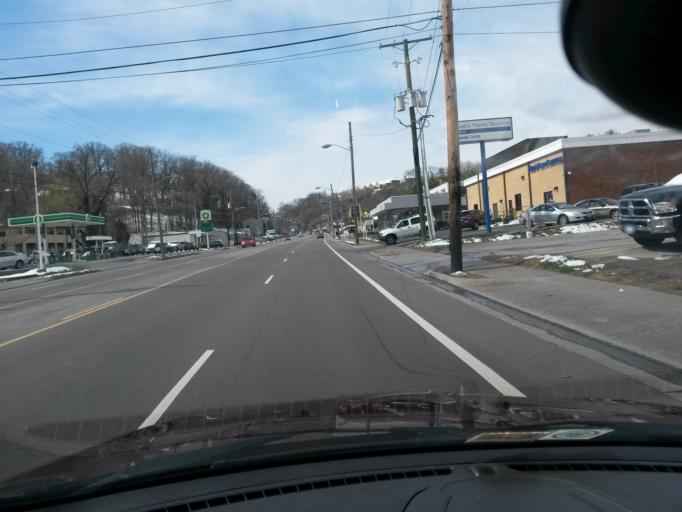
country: US
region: Virginia
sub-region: City of Roanoke
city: Cedar Bluff
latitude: 37.2472
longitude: -79.9590
